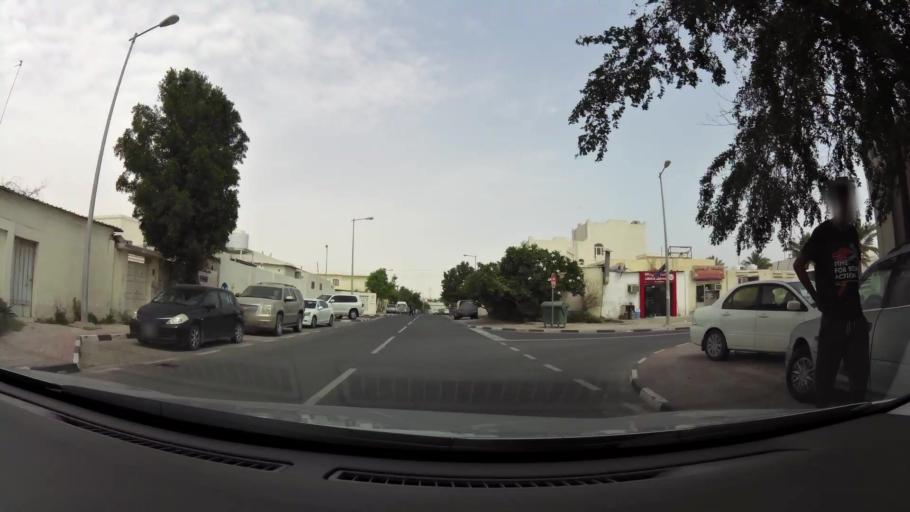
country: QA
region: Baladiyat ad Dawhah
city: Doha
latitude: 25.3126
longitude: 51.4867
